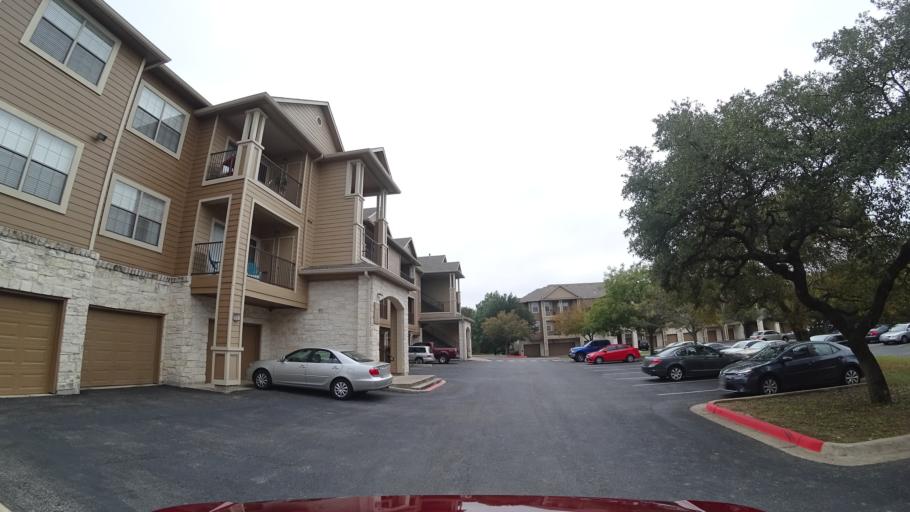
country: US
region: Texas
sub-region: Williamson County
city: Anderson Mill
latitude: 30.4262
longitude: -97.8390
